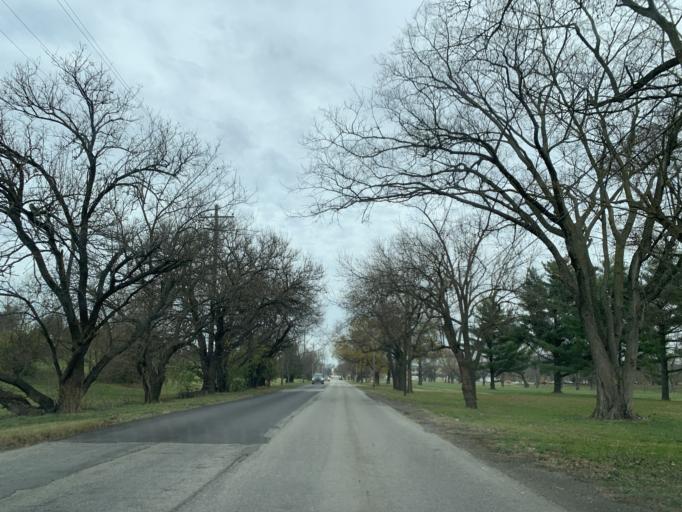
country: US
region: Indiana
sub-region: Clark County
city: Oak Park
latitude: 38.2745
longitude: -85.7038
